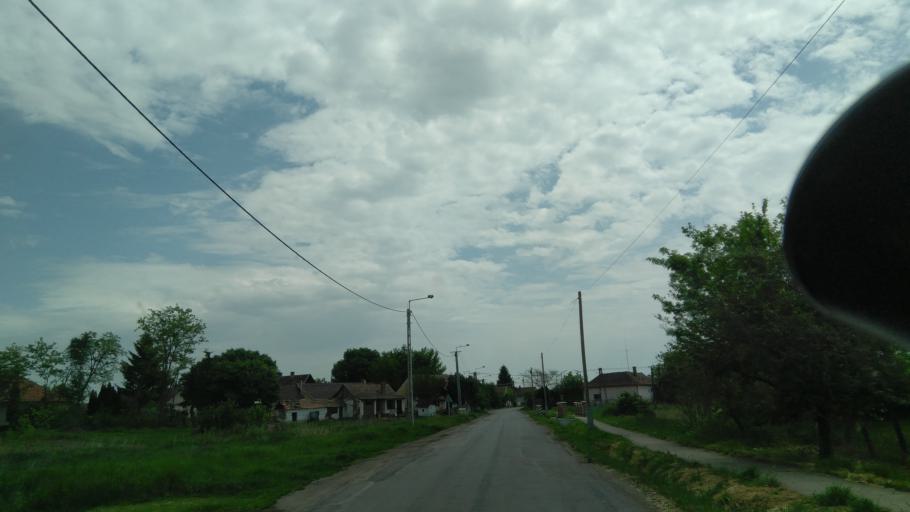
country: HU
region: Hajdu-Bihar
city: Komadi
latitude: 47.0181
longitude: 21.5975
